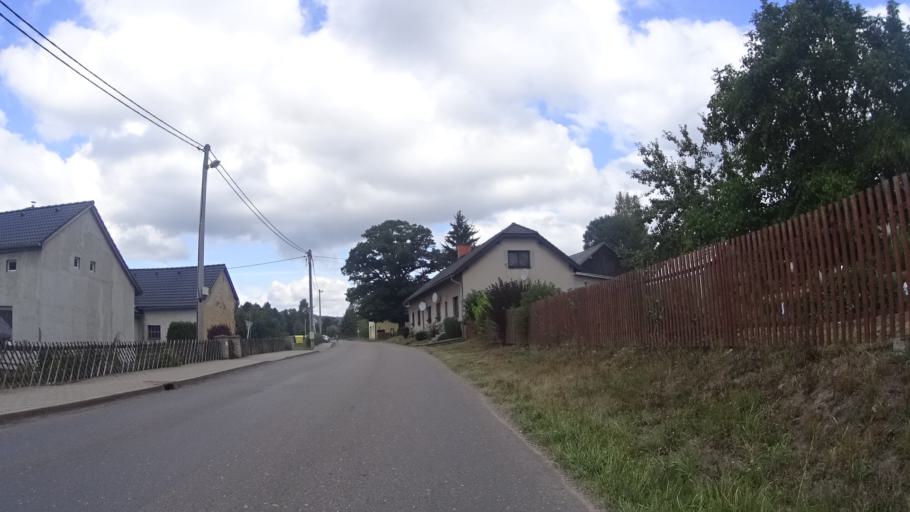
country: CZ
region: Pardubicky
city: Dolni Cermna
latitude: 49.9298
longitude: 16.5412
